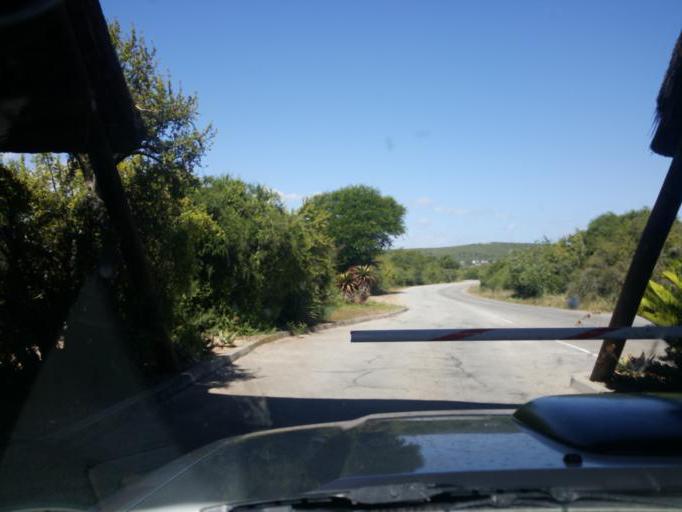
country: ZA
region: Eastern Cape
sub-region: Cacadu District Municipality
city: Kirkwood
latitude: -33.4443
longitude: 25.7387
